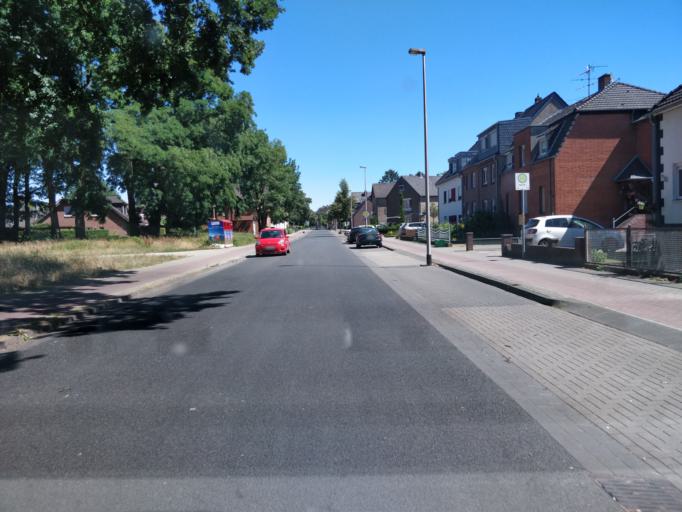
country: DE
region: North Rhine-Westphalia
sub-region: Regierungsbezirk Dusseldorf
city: Emmerich
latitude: 51.8445
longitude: 6.2535
